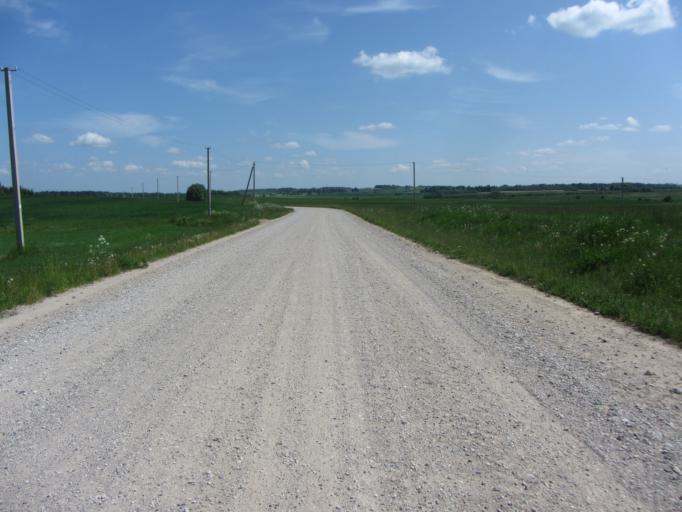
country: LT
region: Vilnius County
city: Elektrenai
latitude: 54.9048
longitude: 24.6039
